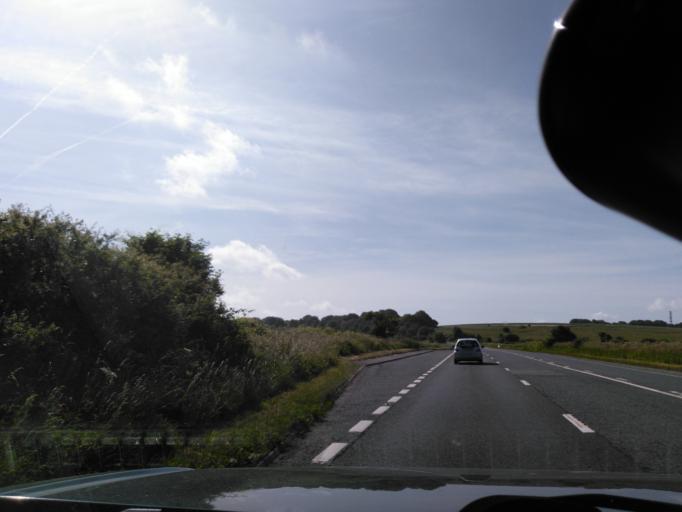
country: GB
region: England
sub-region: Wiltshire
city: Alderbury
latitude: 51.0266
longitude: -1.7110
